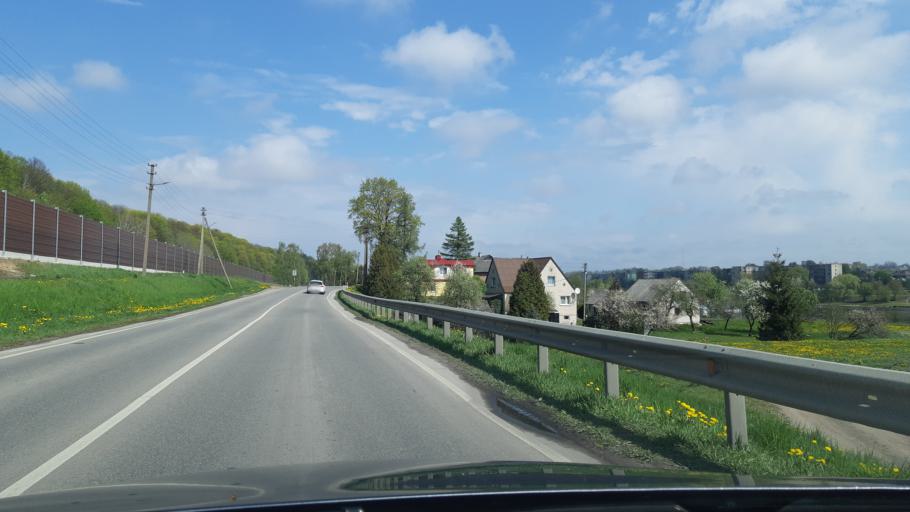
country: LT
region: Kauno apskritis
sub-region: Kaunas
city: Aleksotas
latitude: 54.8626
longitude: 23.9259
